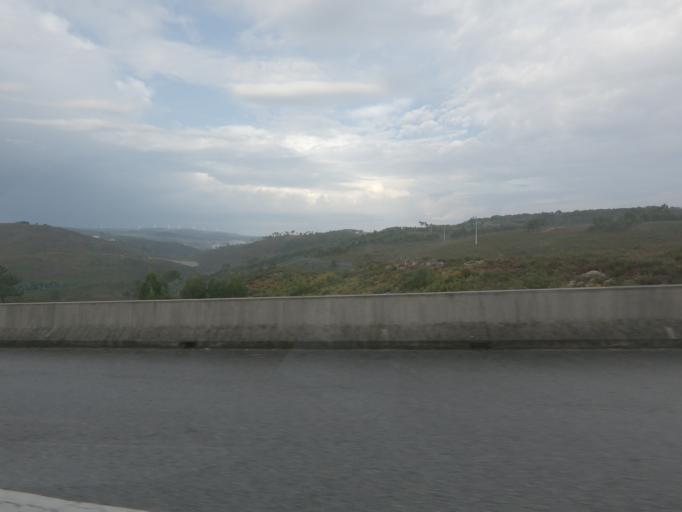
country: PT
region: Viseu
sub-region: Viseu
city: Campo
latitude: 40.7454
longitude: -7.9245
